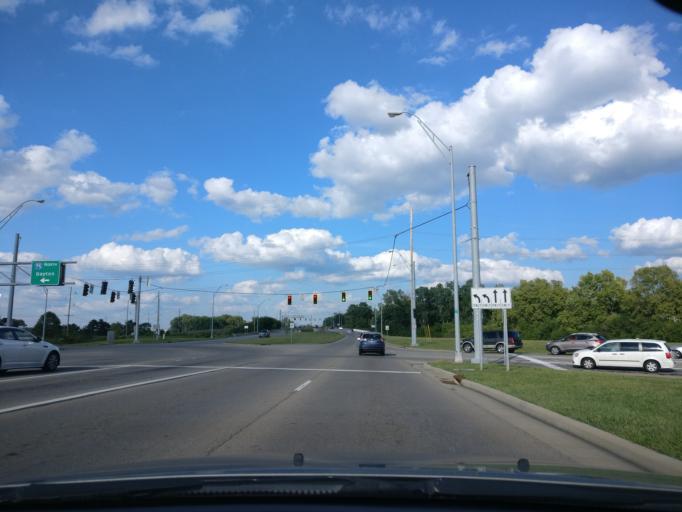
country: US
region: Ohio
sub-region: Montgomery County
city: West Carrollton City
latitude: 39.6815
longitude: -84.2292
